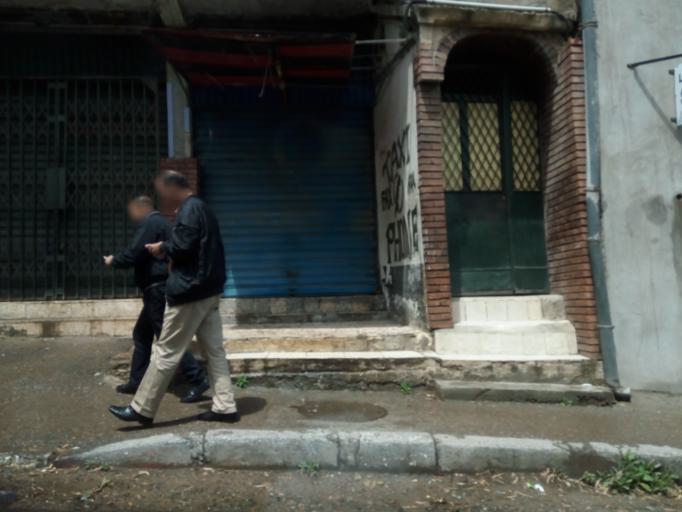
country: DZ
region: Alger
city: Algiers
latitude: 36.7770
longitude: 3.0491
